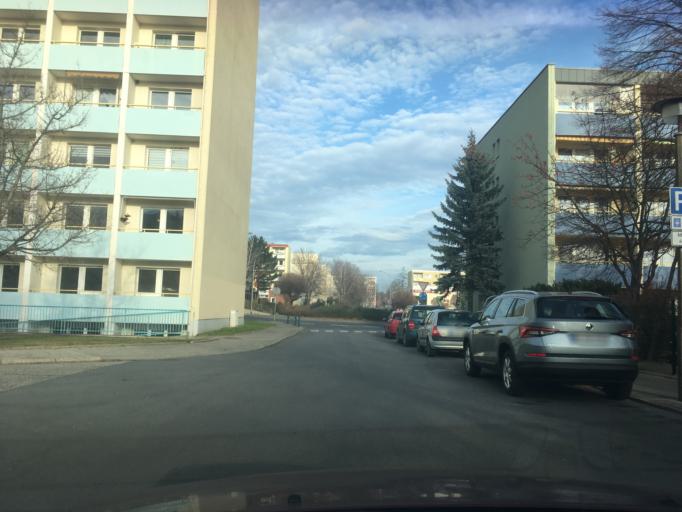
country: DE
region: Saxony
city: Bautzen
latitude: 51.1745
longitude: 14.4539
